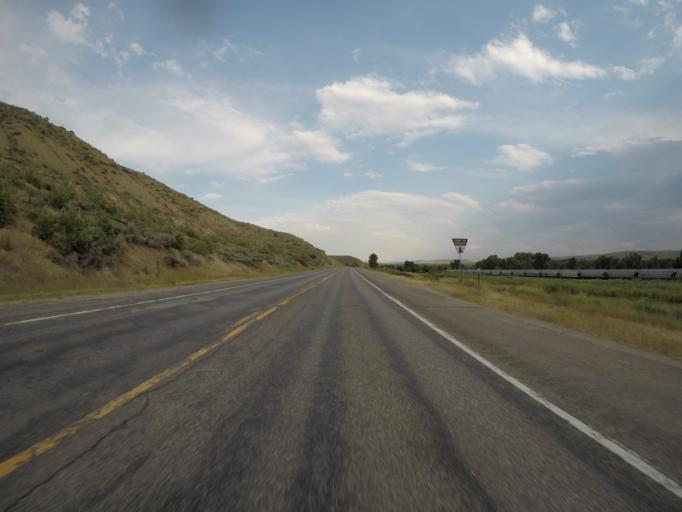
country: US
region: Colorado
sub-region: Routt County
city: Hayden
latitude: 40.5088
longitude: -107.3823
